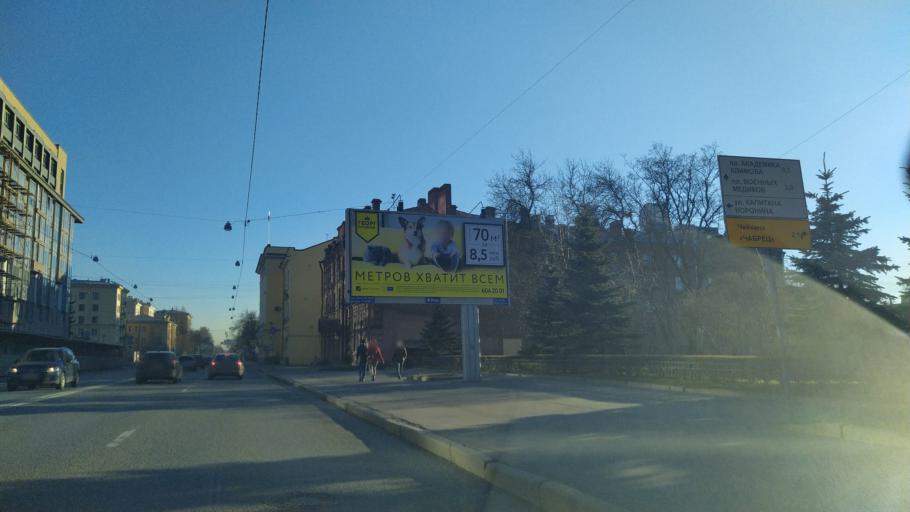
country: RU
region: Leningrad
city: Sampsonievskiy
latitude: 59.9872
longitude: 30.3341
